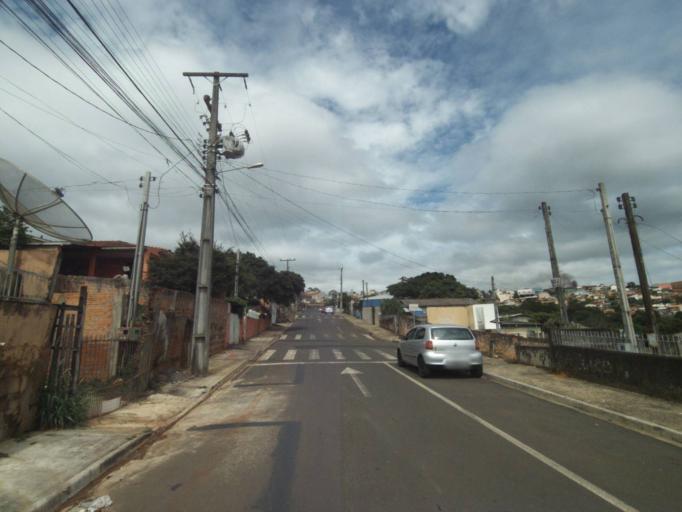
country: BR
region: Parana
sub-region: Telemaco Borba
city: Telemaco Borba
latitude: -24.3327
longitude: -50.6393
